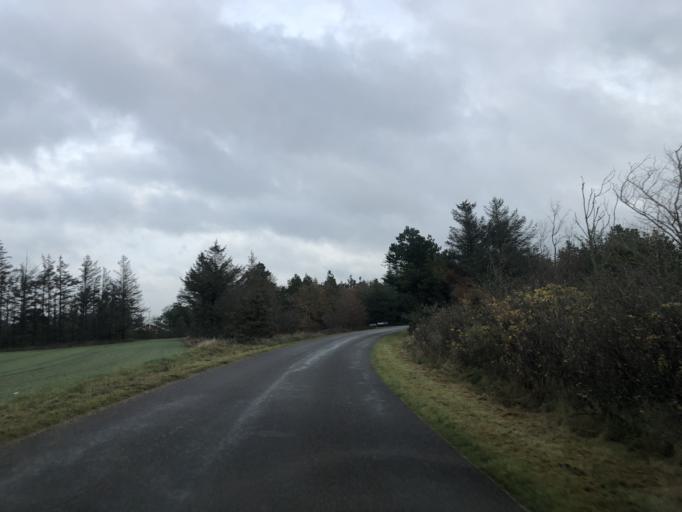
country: DK
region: Central Jutland
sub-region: Holstebro Kommune
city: Ulfborg
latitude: 56.3133
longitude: 8.2158
